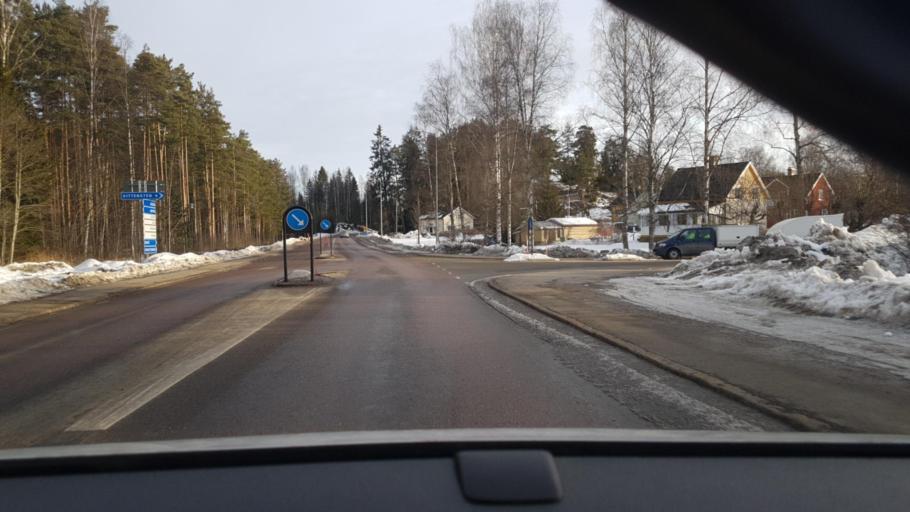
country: SE
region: Vaermland
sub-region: Eda Kommun
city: Amotfors
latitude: 59.7699
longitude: 12.3657
